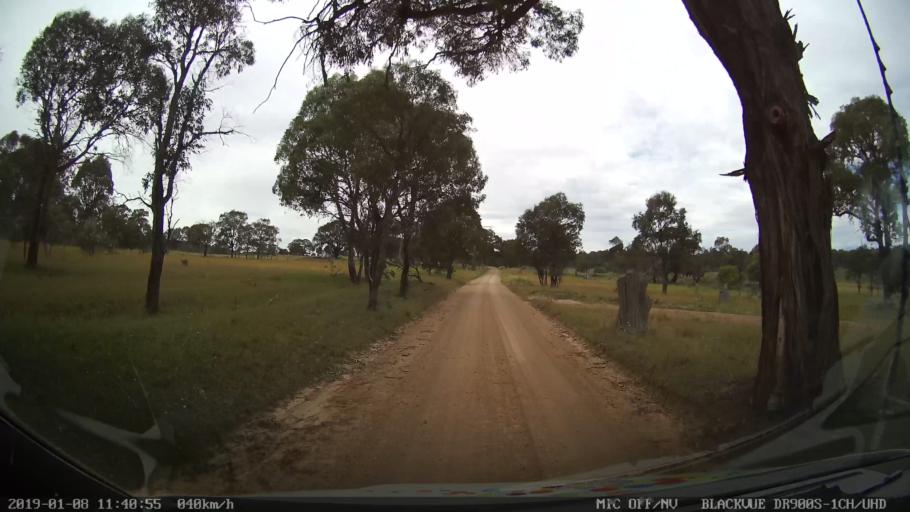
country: AU
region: New South Wales
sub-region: Armidale Dumaresq
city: Armidale
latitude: -30.3758
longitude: 151.5646
